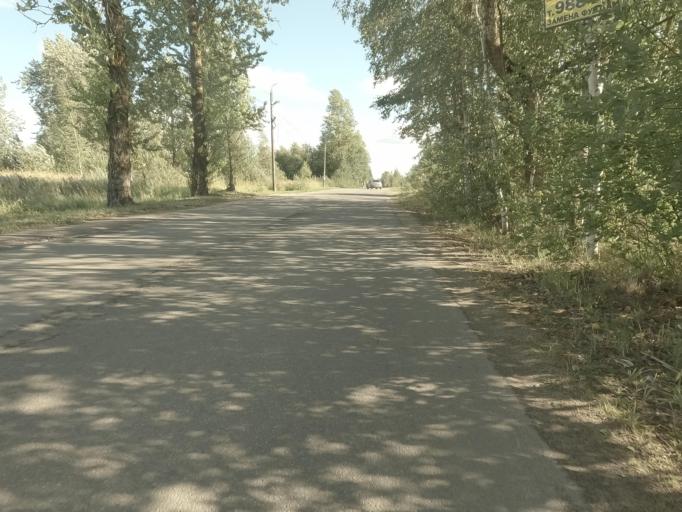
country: RU
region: Leningrad
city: Imeni Morozova
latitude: 59.9680
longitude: 31.0283
